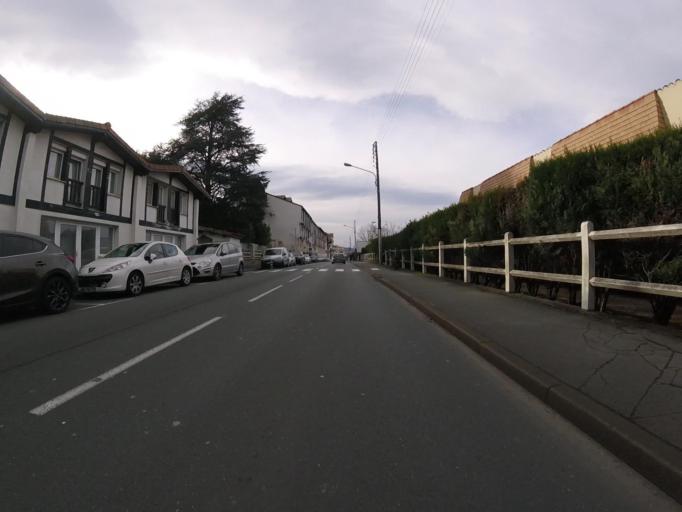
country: FR
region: Aquitaine
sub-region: Departement des Pyrenees-Atlantiques
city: Hendaye
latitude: 43.3548
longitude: -1.7789
